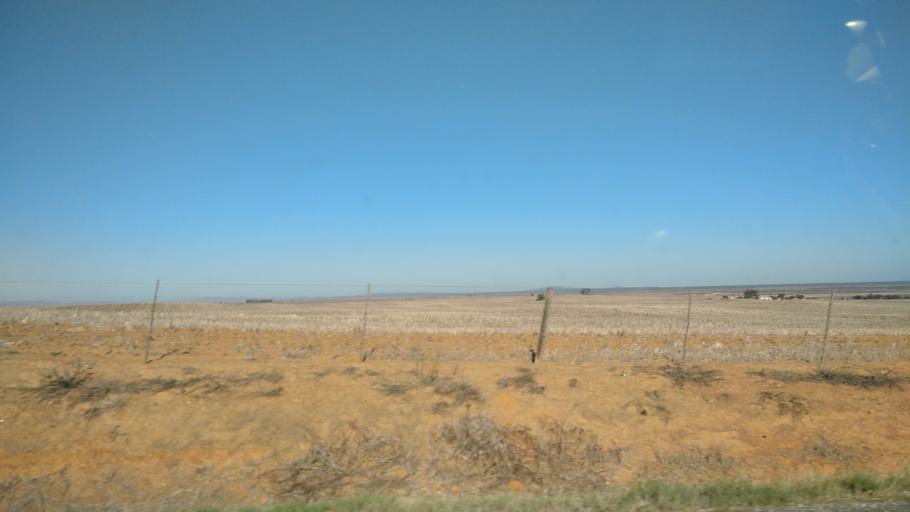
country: ZA
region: Western Cape
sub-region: West Coast District Municipality
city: Moorreesburg
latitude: -33.1595
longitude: 18.4710
